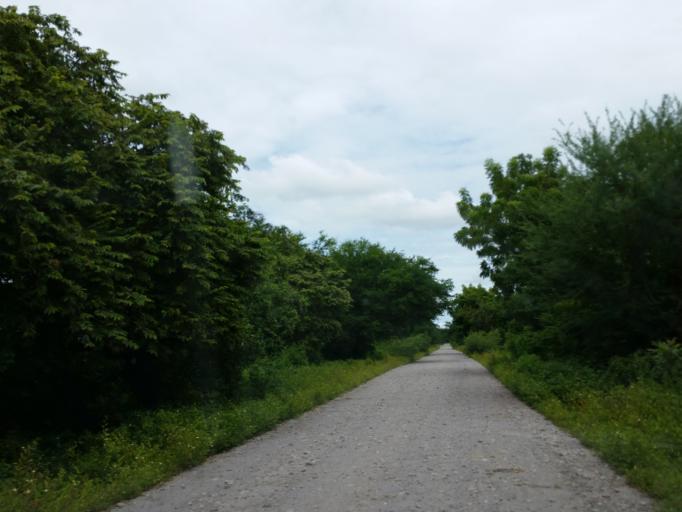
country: NI
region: Leon
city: Telica
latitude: 12.6989
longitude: -86.8688
